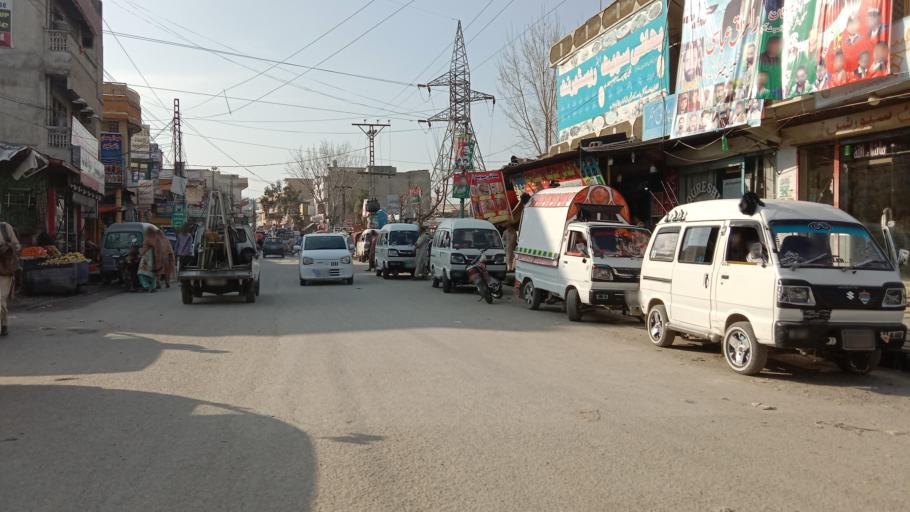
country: PK
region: Khyber Pakhtunkhwa
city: Abbottabad
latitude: 34.1962
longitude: 73.2344
